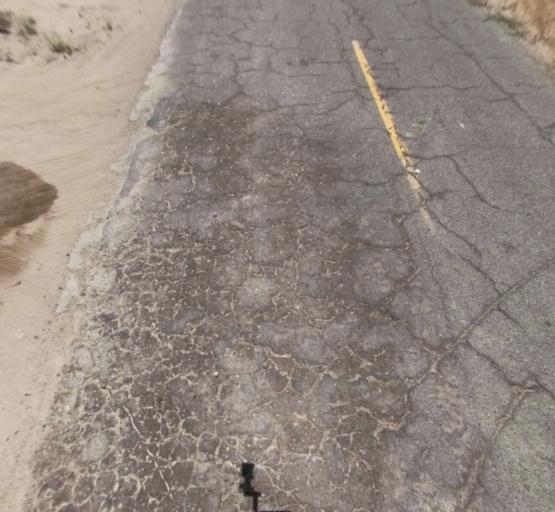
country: US
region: California
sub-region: Fresno County
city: Biola
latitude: 36.8405
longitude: -120.0921
